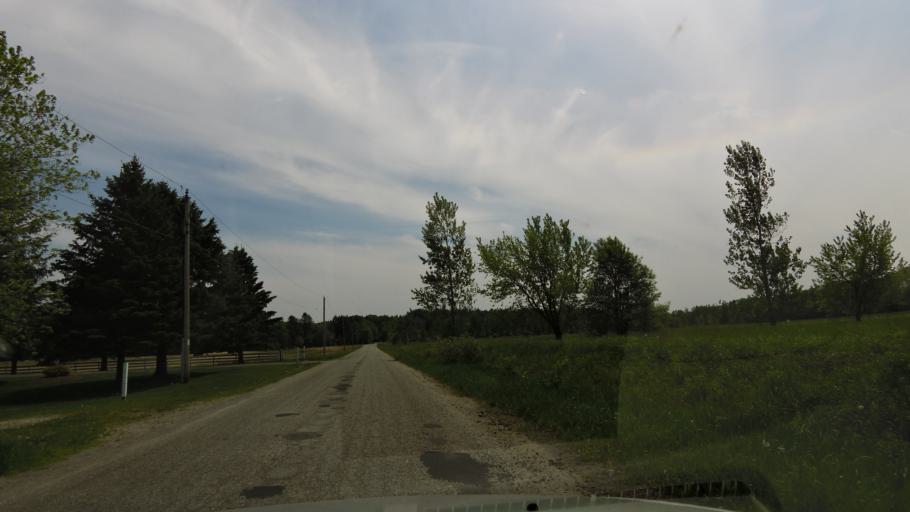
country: CA
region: Ontario
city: Cobourg
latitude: 43.9833
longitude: -78.4790
